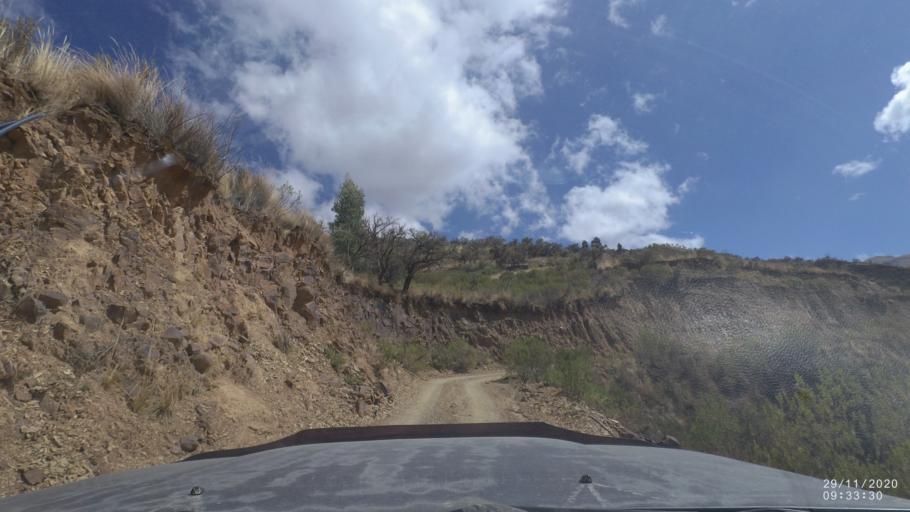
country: BO
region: Cochabamba
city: Cochabamba
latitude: -17.3122
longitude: -66.1882
